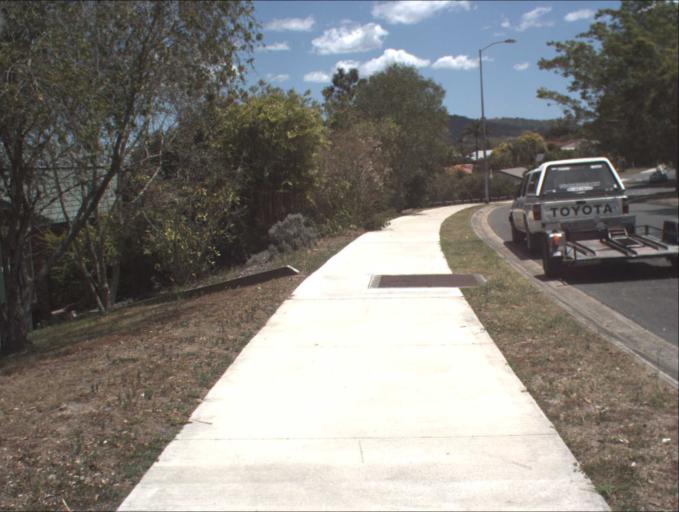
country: AU
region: Queensland
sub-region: Logan
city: Windaroo
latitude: -27.7362
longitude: 153.2053
